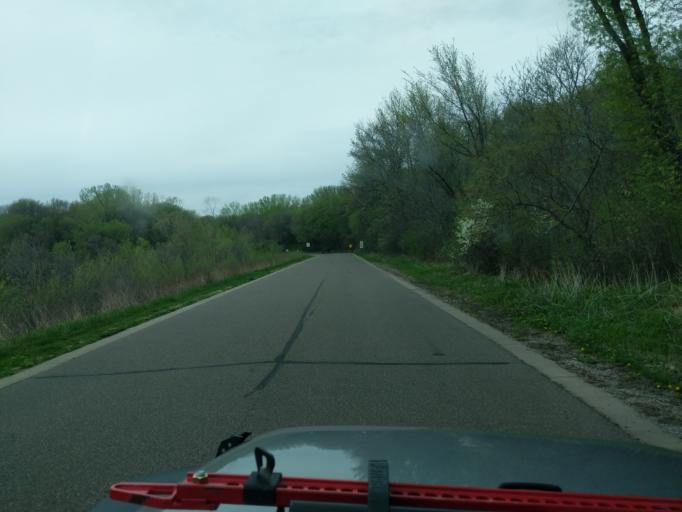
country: US
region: Minnesota
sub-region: Anoka County
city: Coon Rapids
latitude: 45.1419
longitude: -93.2986
